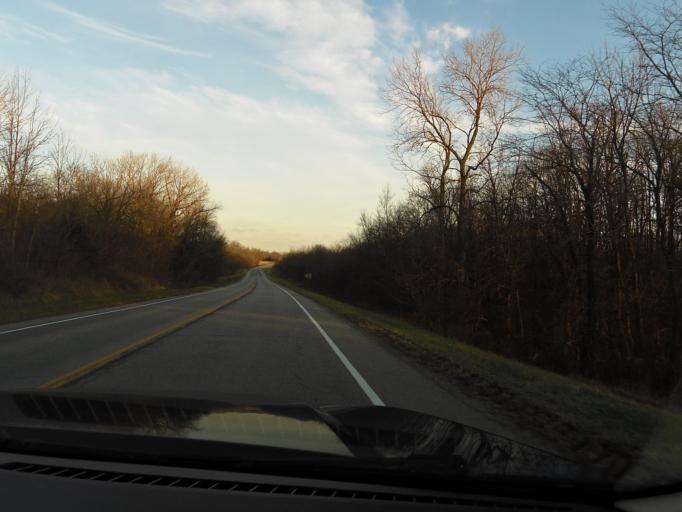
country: US
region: Illinois
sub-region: Fayette County
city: Vandalia
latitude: 38.8155
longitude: -89.0865
